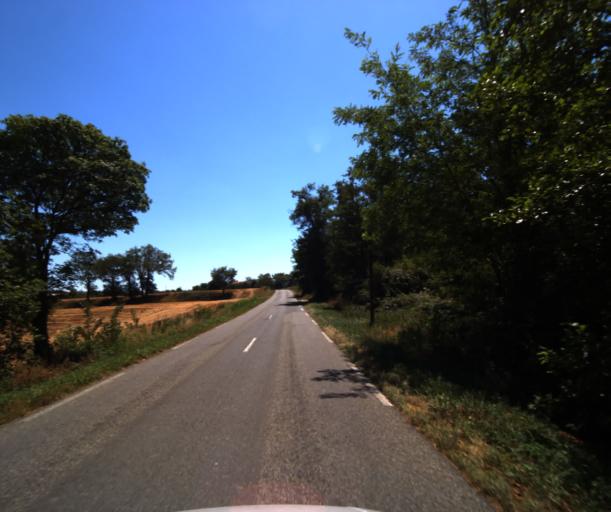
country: FR
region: Midi-Pyrenees
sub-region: Departement de la Haute-Garonne
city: Seysses
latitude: 43.4553
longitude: 1.2925
